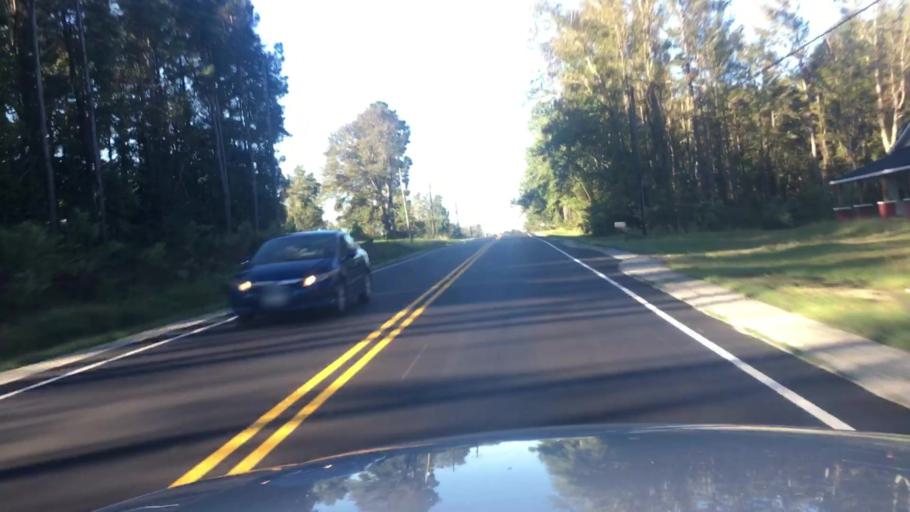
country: US
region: North Carolina
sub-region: Harnett County
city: Walkertown
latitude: 35.3171
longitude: -78.8790
